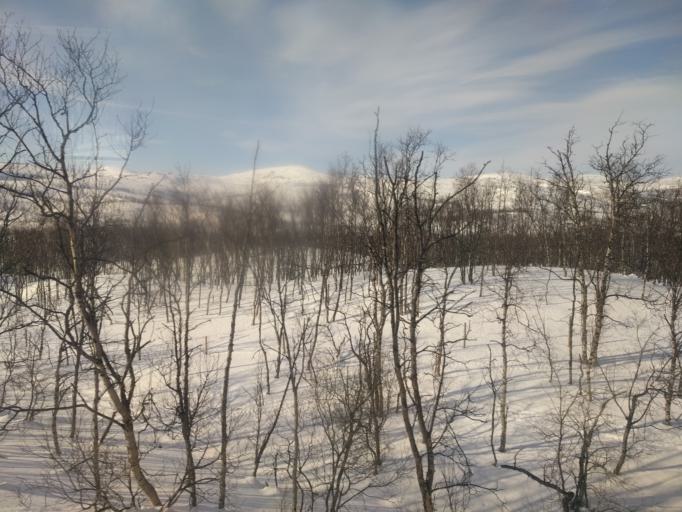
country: NO
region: Troms
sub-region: Bardu
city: Setermoen
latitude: 68.4262
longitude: 18.4574
